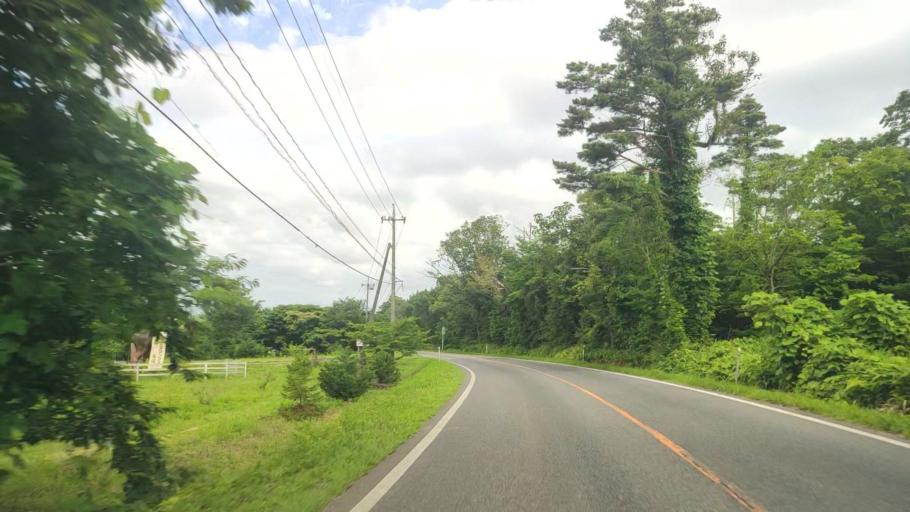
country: JP
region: Tottori
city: Yonago
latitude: 35.4133
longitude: 133.4684
